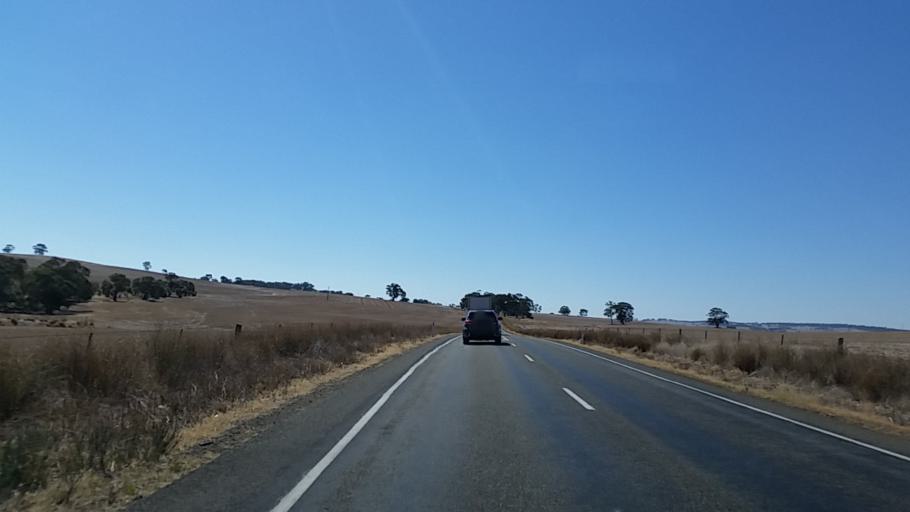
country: AU
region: South Australia
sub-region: Clare and Gilbert Valleys
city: Clare
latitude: -34.0435
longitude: 138.7996
